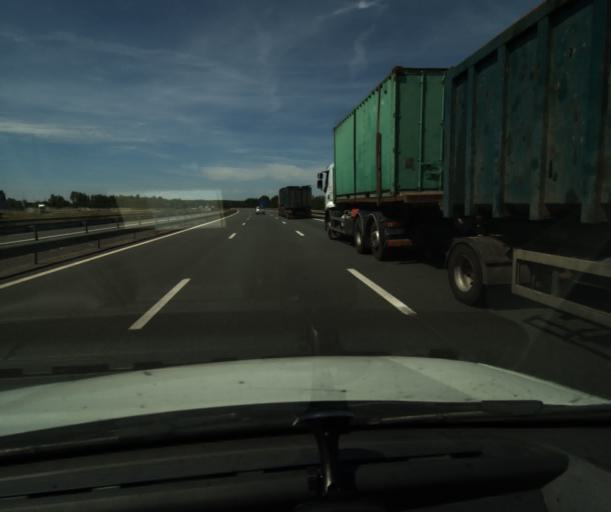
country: FR
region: Midi-Pyrenees
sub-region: Departement du Tarn-et-Garonne
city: Campsas
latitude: 43.9153
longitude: 1.3191
